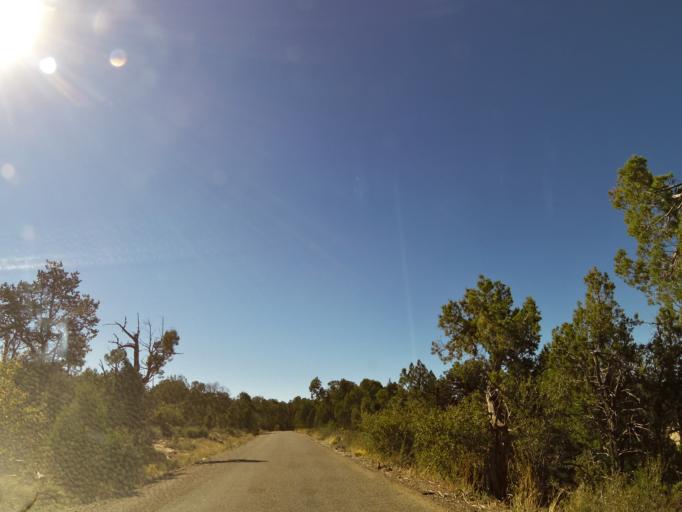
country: US
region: Colorado
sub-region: Montezuma County
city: Cortez
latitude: 37.1650
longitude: -108.4801
